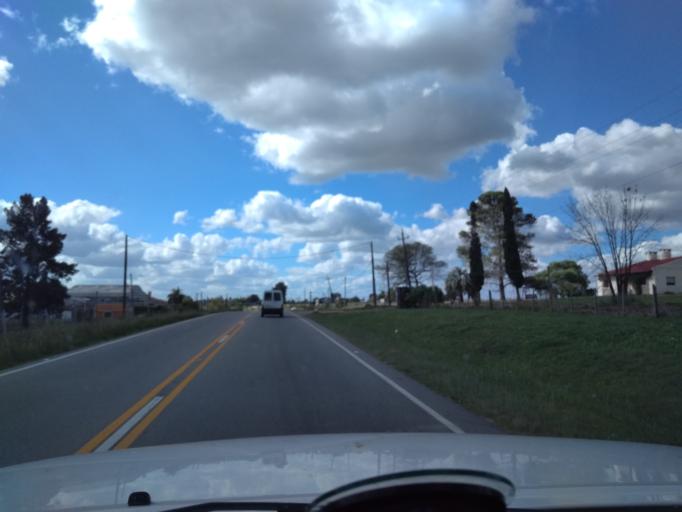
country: UY
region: Canelones
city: Joaquin Suarez
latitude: -34.6929
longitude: -56.0551
